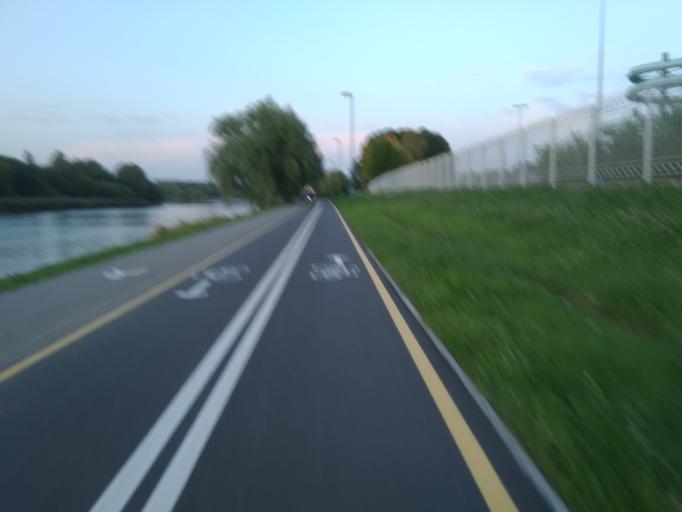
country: BY
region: Minsk
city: Minsk
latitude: 53.9326
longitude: 27.5168
